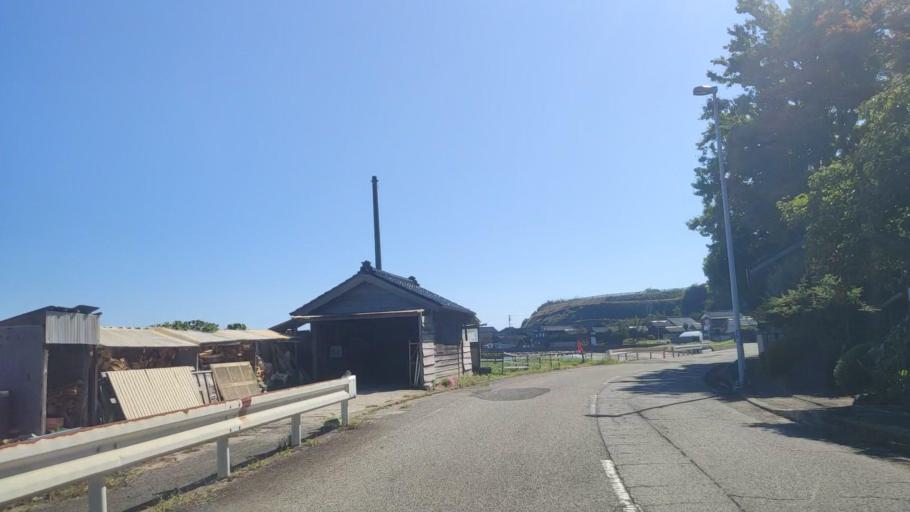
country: JP
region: Toyama
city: Nyuzen
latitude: 37.5009
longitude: 137.3492
